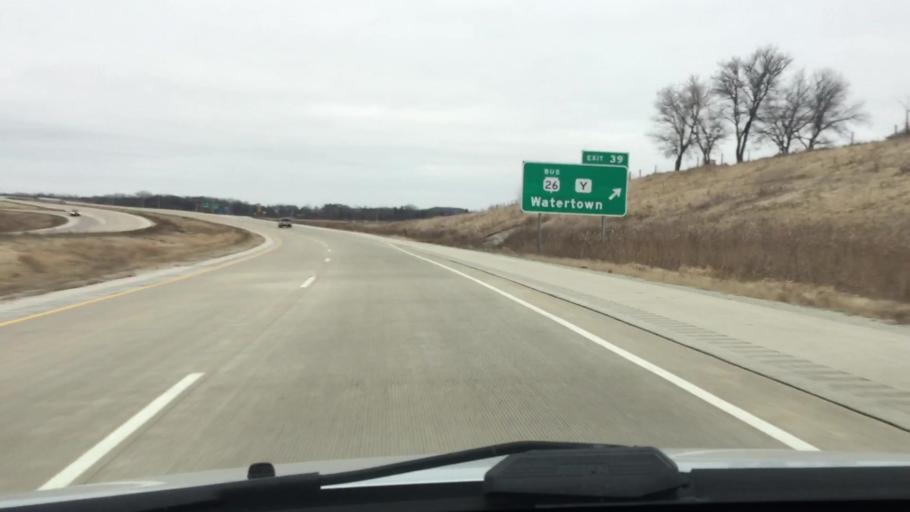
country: US
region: Wisconsin
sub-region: Jefferson County
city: Watertown
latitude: 43.1522
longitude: -88.7361
